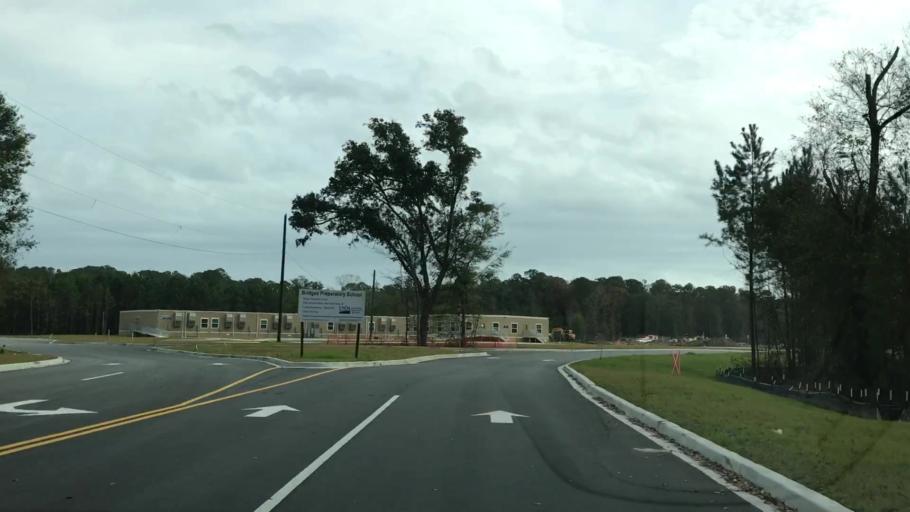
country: US
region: South Carolina
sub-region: Beaufort County
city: Burton
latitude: 32.4150
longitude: -80.7479
